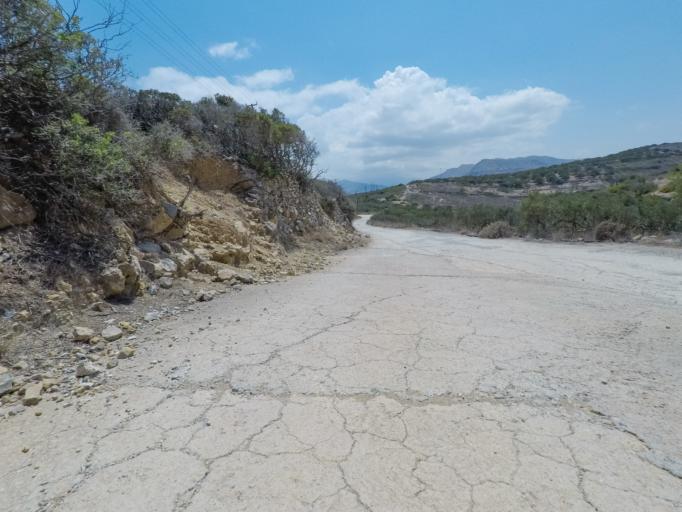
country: GR
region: Crete
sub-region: Nomos Lasithiou
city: Elounda
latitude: 35.3188
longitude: 25.7483
